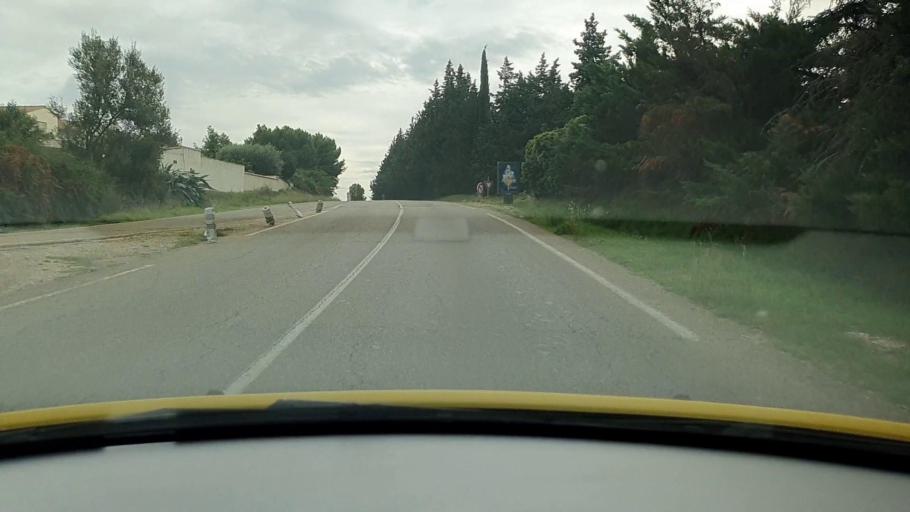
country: FR
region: Languedoc-Roussillon
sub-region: Departement du Gard
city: Saint-Gilles
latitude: 43.6810
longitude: 4.4346
